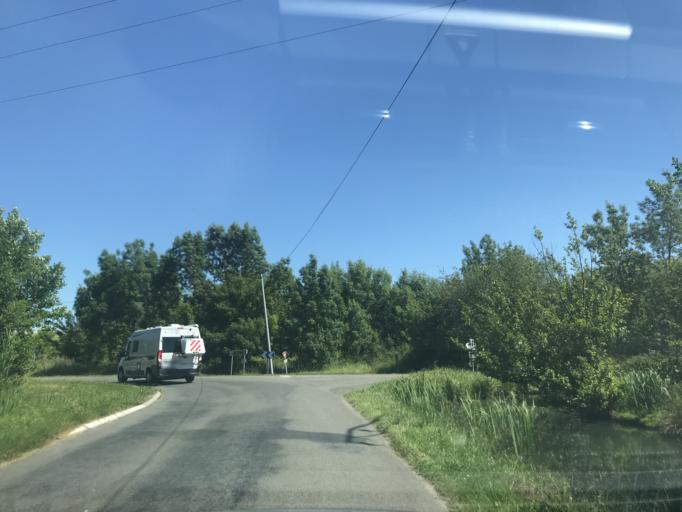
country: FR
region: Poitou-Charentes
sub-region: Departement de la Charente-Maritime
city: Mortagne-sur-Gironde
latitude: 45.4245
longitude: -0.7401
